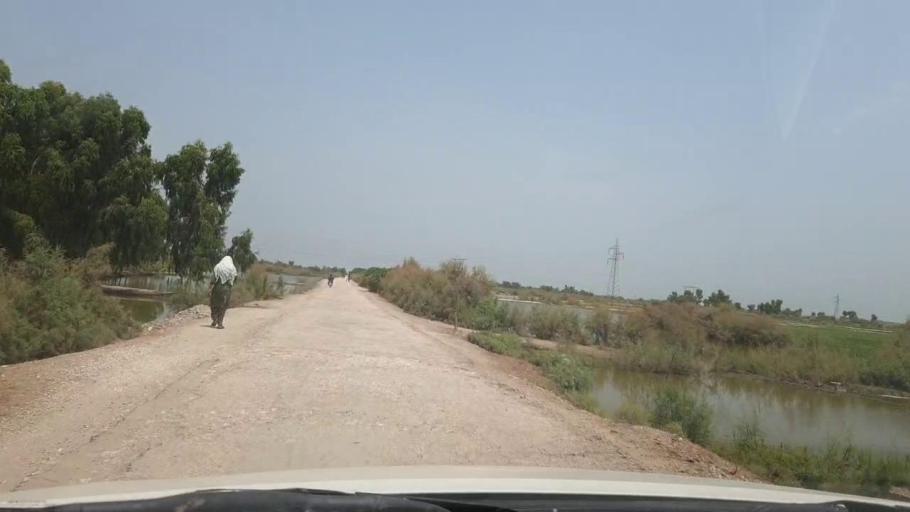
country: PK
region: Sindh
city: Rustam jo Goth
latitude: 28.0251
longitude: 68.8129
